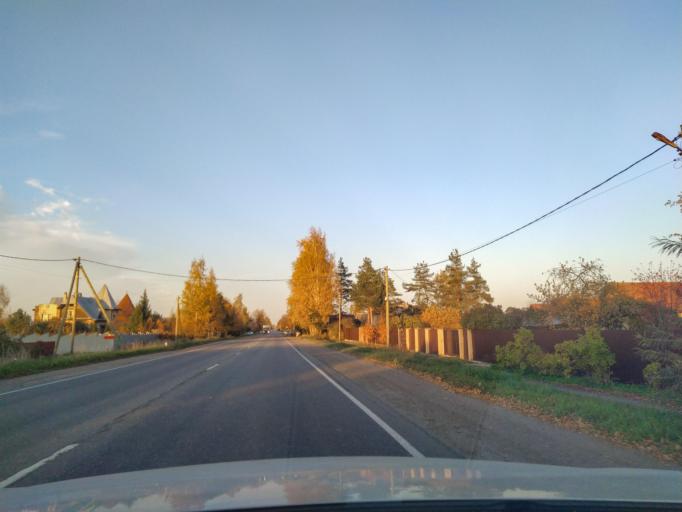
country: RU
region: Leningrad
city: Maloye Verevo
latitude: 59.6131
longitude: 30.2015
